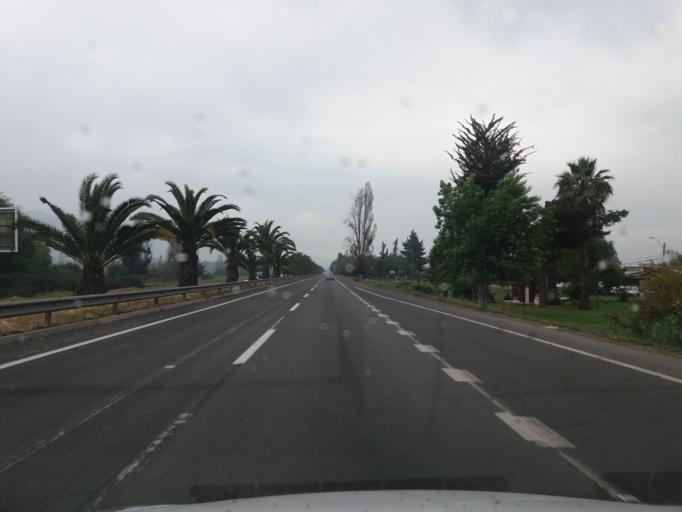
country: CL
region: Valparaiso
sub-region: Provincia de Quillota
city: Hacienda La Calera
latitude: -32.7798
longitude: -71.1785
